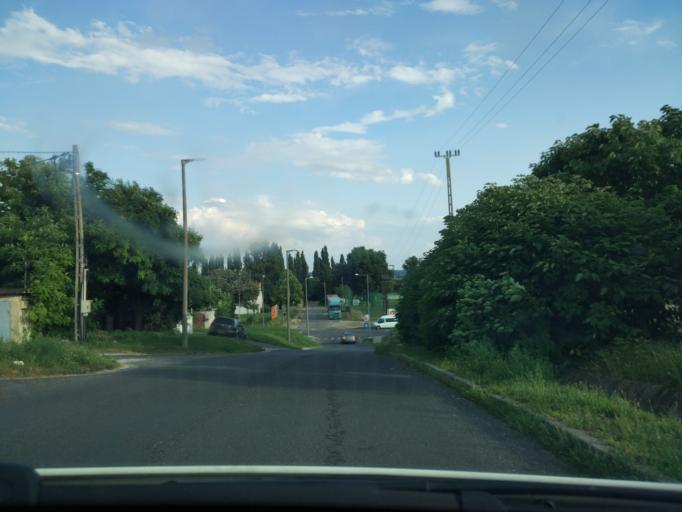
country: HU
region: Veszprem
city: Varpalota
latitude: 47.2012
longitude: 18.1476
